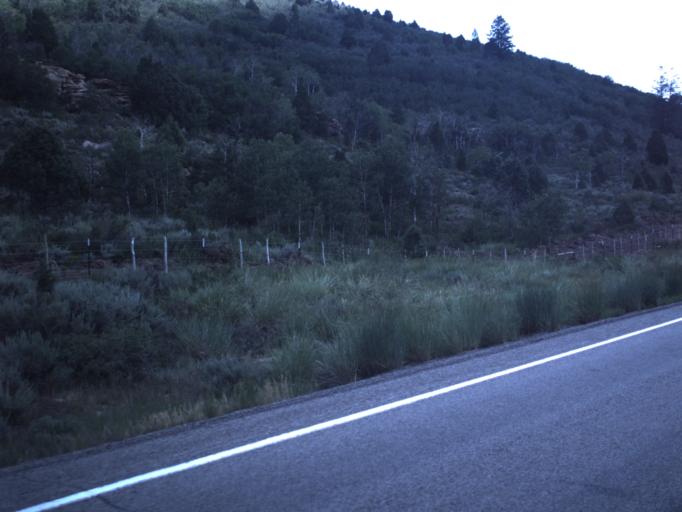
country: US
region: Utah
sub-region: Carbon County
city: Helper
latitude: 39.8573
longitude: -111.0939
